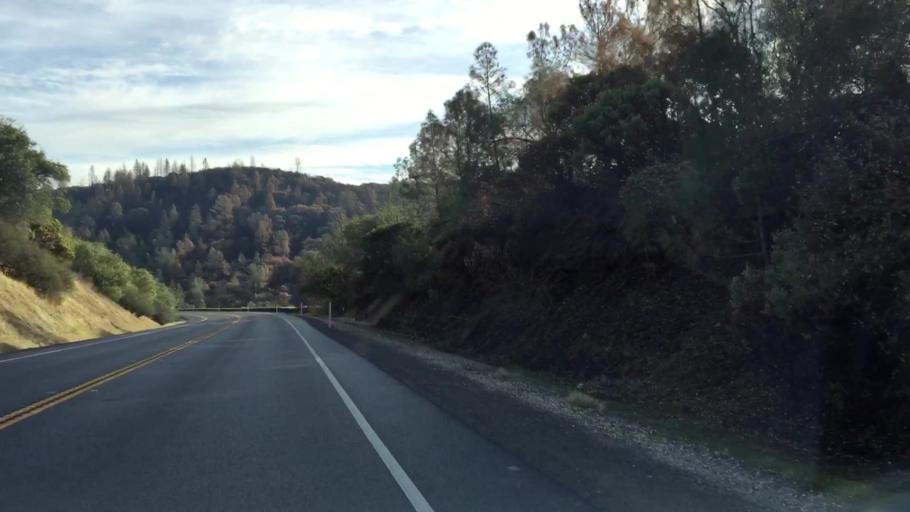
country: US
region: California
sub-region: Butte County
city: Paradise
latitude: 39.6543
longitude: -121.5450
